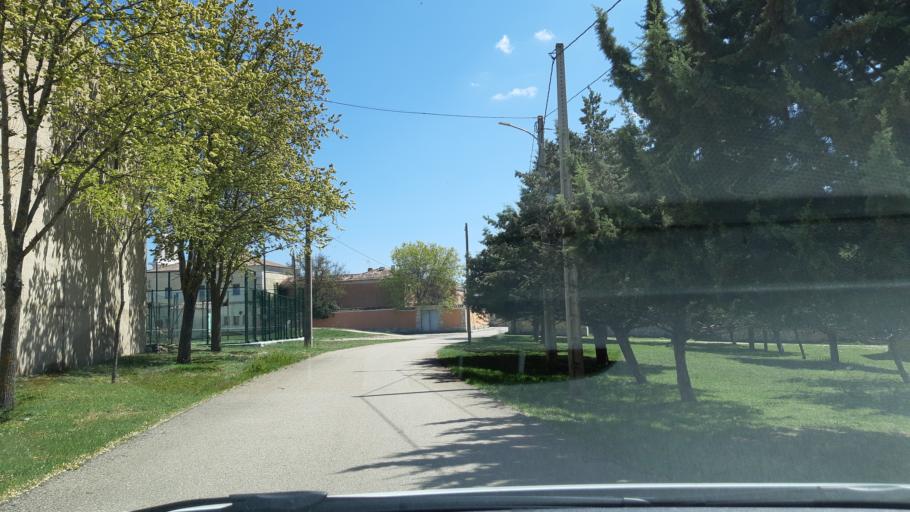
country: ES
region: Castille-La Mancha
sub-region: Provincia de Guadalajara
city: Gajanejos
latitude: 40.8430
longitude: -2.8936
